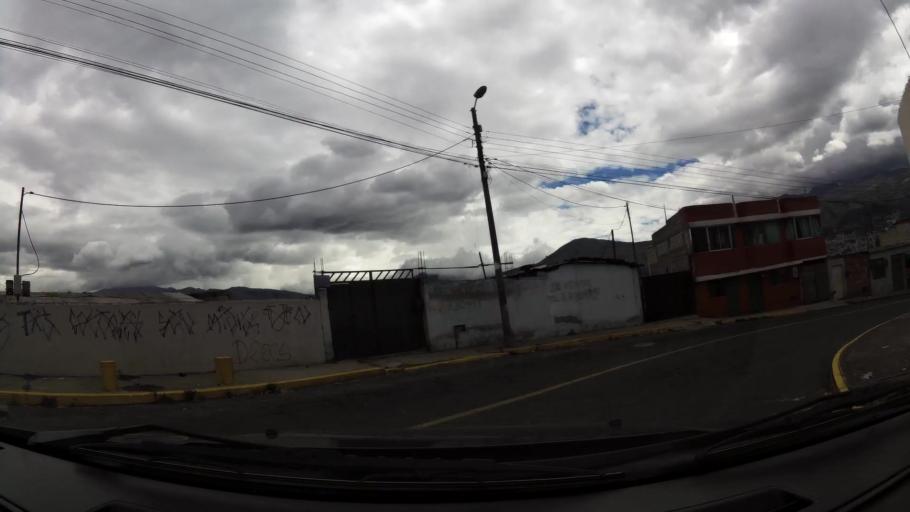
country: EC
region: Pichincha
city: Quito
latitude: -0.2510
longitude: -78.5085
